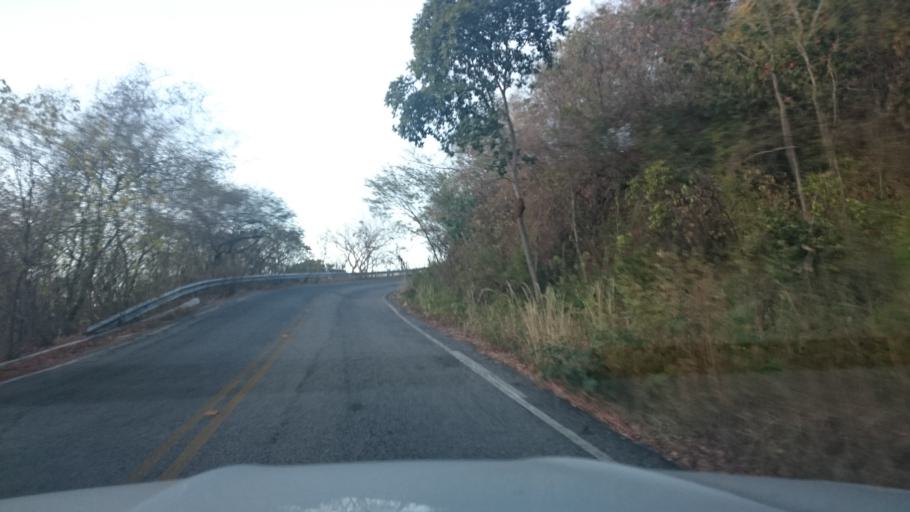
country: BR
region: Rio Grande do Norte
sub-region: Umarizal
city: Umarizal
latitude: -6.0193
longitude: -37.9913
